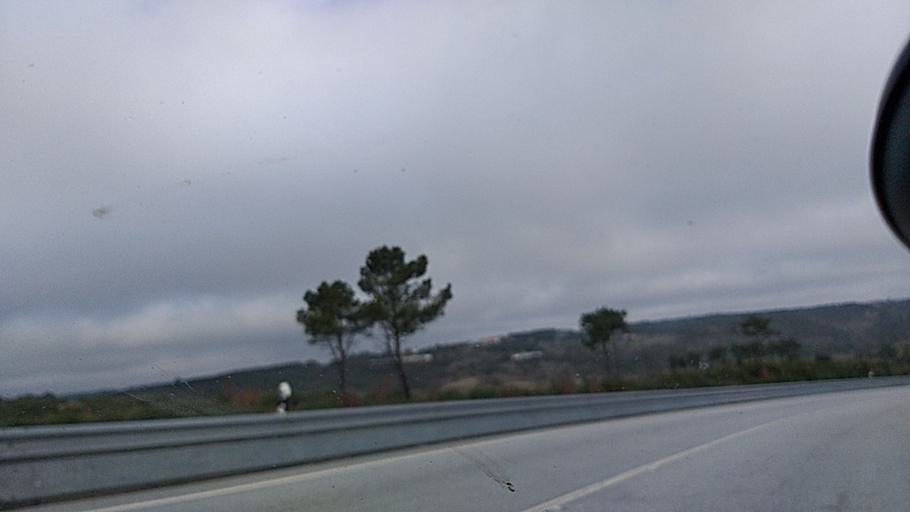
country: PT
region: Guarda
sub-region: Aguiar da Beira
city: Aguiar da Beira
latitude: 40.7723
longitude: -7.5046
